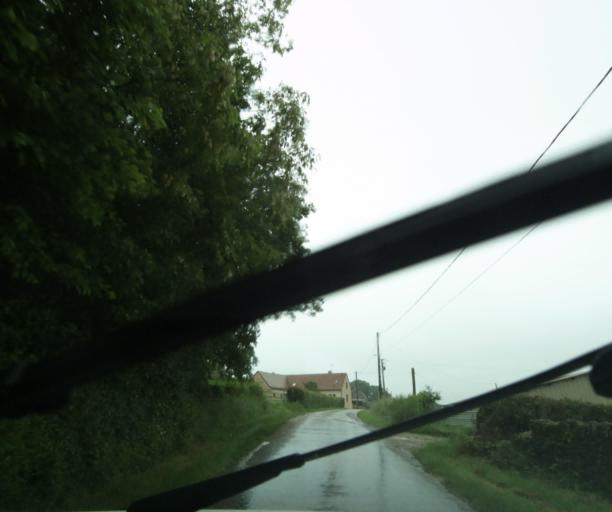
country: FR
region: Bourgogne
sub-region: Departement de Saone-et-Loire
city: Charolles
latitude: 46.4042
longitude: 4.2485
